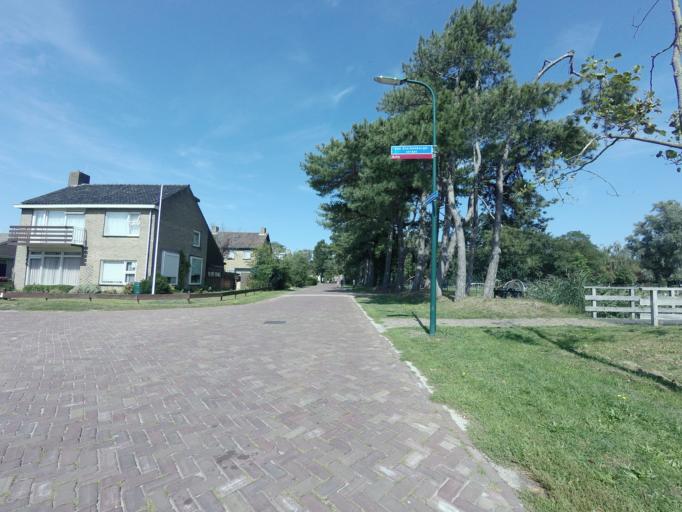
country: NL
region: Friesland
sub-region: Gemeente Schiermonnikoog
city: Schiermonnikoog
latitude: 53.4788
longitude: 6.1660
